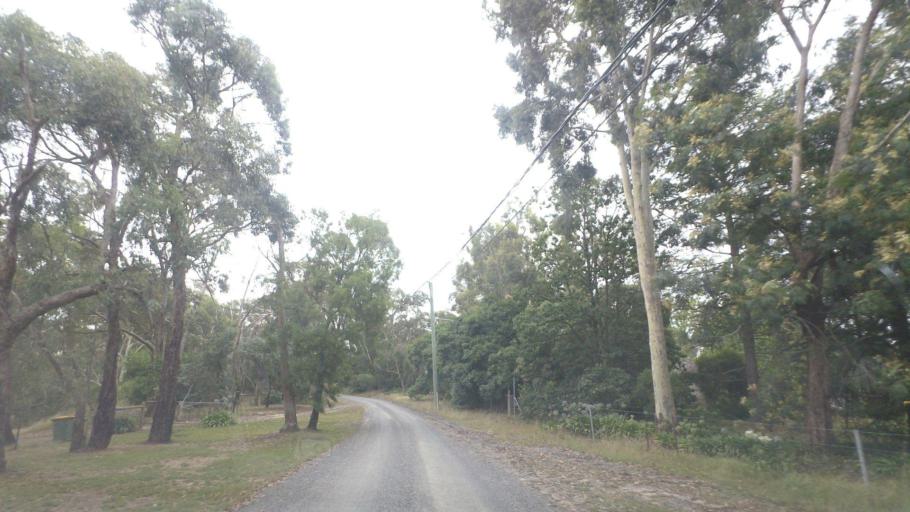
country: AU
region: Victoria
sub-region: Yarra Ranges
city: Mount Evelyn
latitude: -37.7582
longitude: 145.3988
